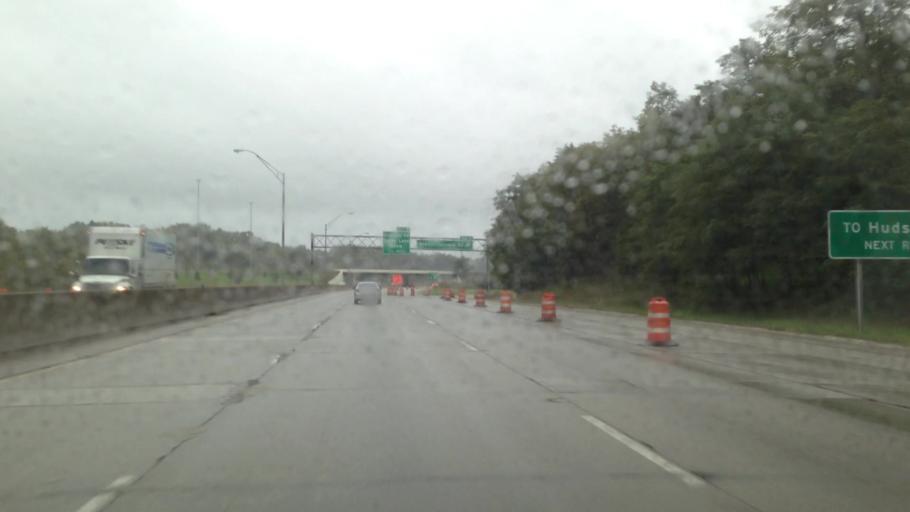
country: US
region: Ohio
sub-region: Summit County
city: Silver Lake
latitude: 41.1849
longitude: -81.4779
